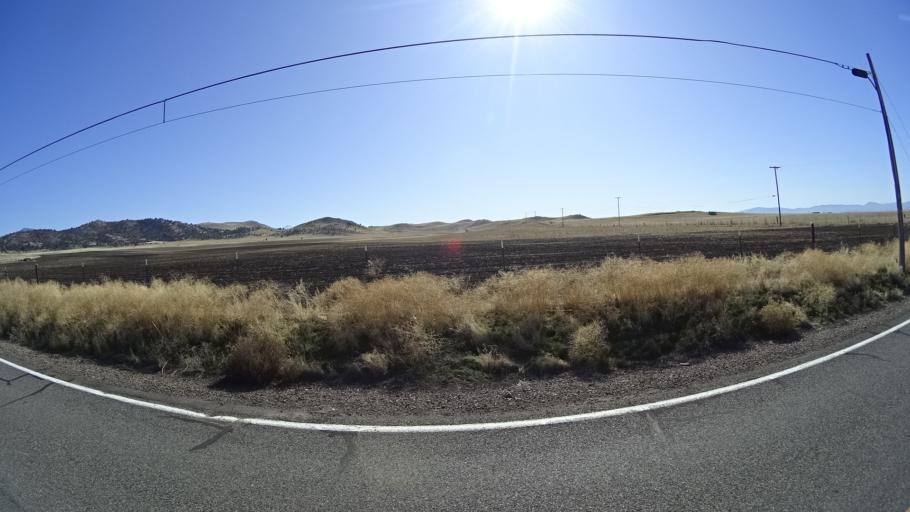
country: US
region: California
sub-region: Siskiyou County
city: Montague
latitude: 41.8047
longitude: -122.4153
